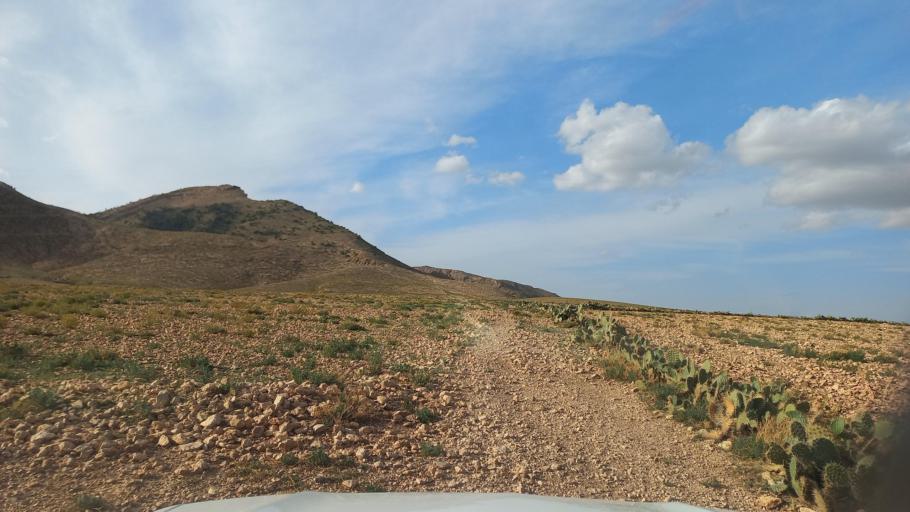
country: TN
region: Al Qasrayn
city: Sbiba
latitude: 35.4583
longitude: 9.0769
